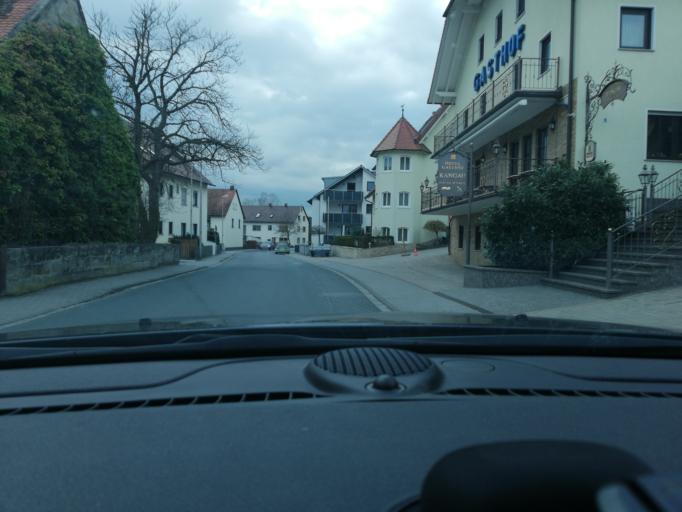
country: DE
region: Bavaria
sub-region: Regierungsbezirk Mittelfranken
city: Hessdorf
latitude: 49.6291
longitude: 10.9388
